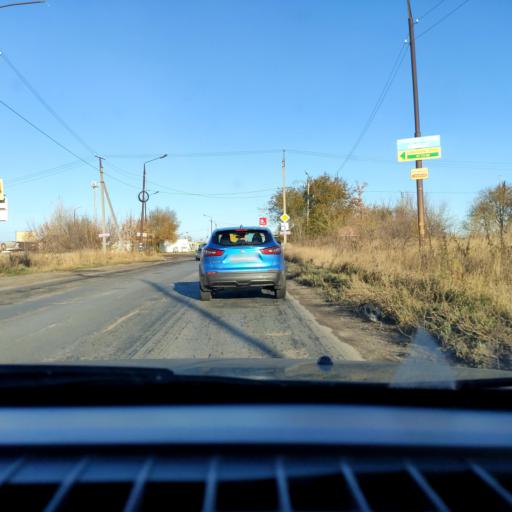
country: RU
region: Samara
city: Tol'yatti
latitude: 53.5735
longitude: 49.3404
